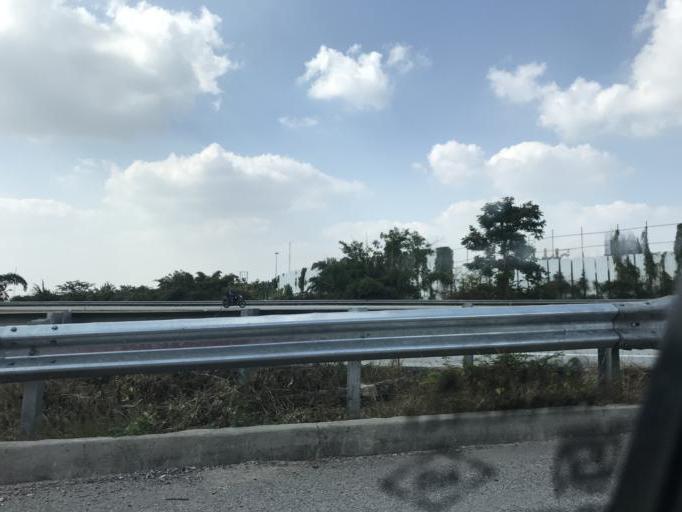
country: IN
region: Karnataka
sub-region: Bangalore Urban
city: Bangalore
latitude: 12.8801
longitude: 77.4966
